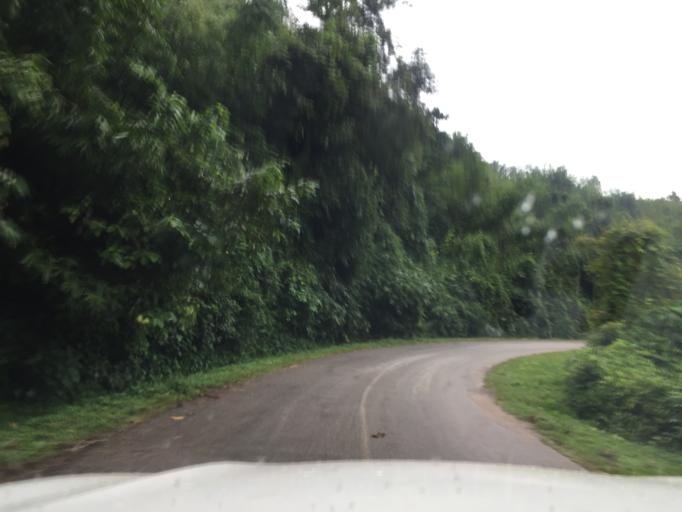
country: LA
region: Oudomxai
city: Muang La
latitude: 20.8281
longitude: 102.0979
